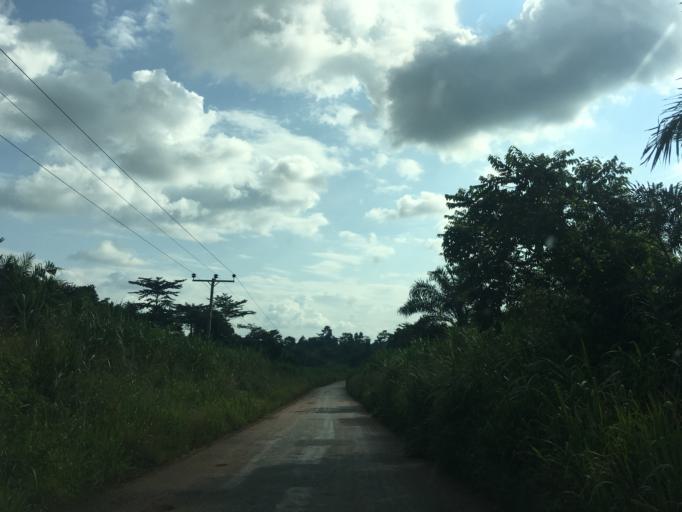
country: GH
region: Western
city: Bibiani
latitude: 6.7830
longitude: -2.5473
